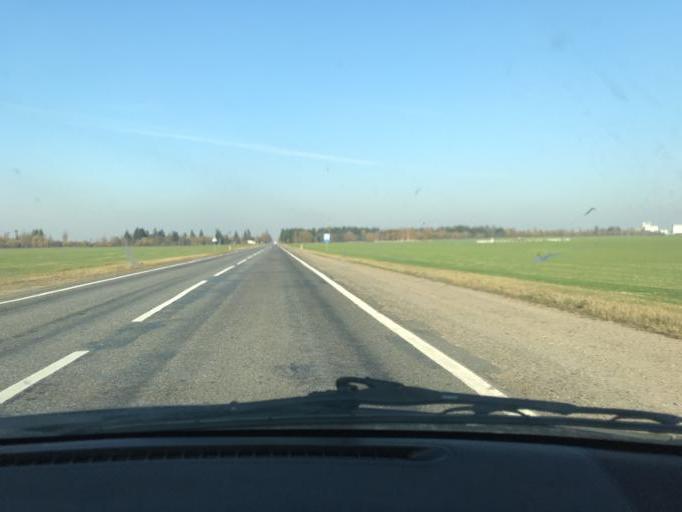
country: BY
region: Vitebsk
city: Orsha
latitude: 54.4442
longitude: 30.4877
